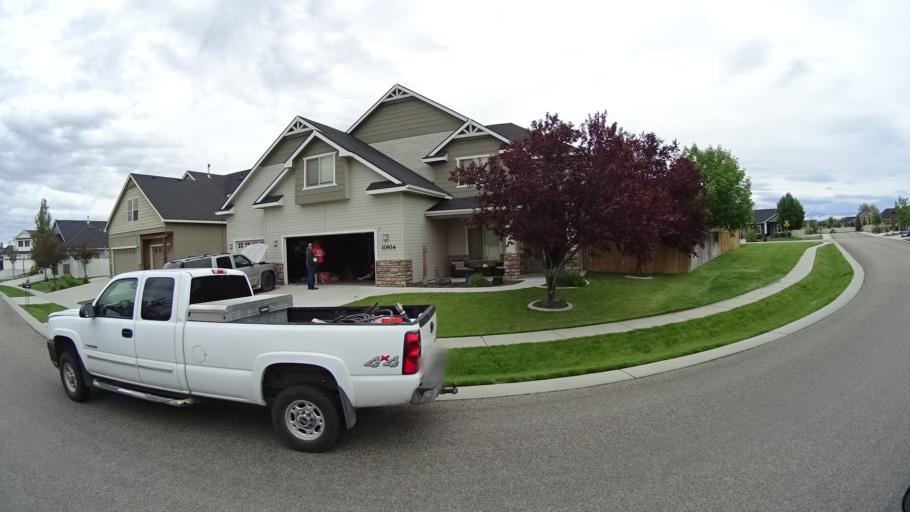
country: US
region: Idaho
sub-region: Ada County
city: Star
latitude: 43.7005
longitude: -116.4890
